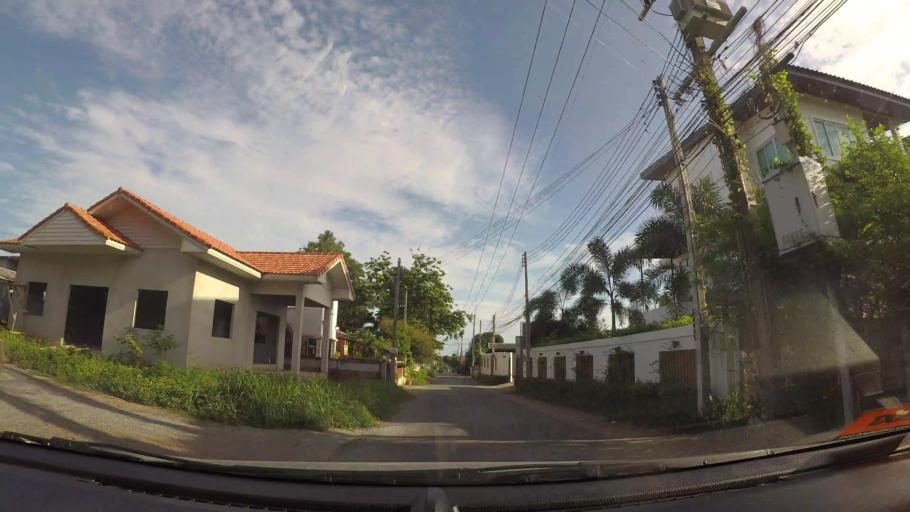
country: TH
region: Chon Buri
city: Sattahip
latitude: 12.6748
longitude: 100.9170
